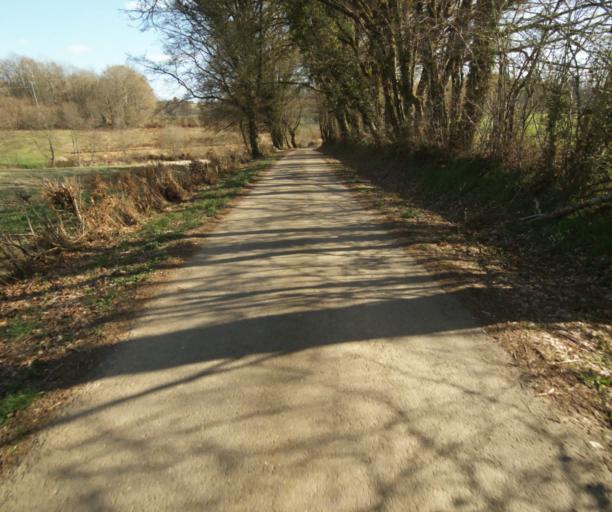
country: FR
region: Limousin
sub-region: Departement de la Correze
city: Saint-Mexant
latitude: 45.3244
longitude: 1.6166
